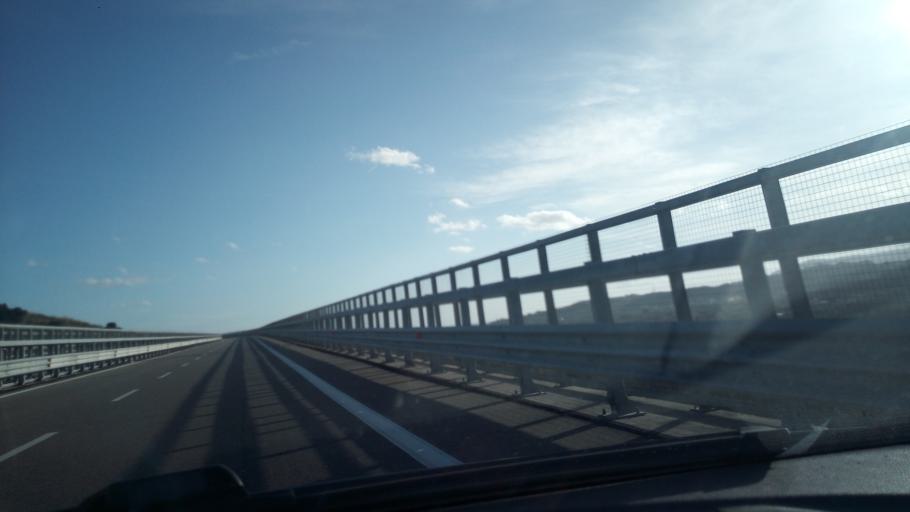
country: IT
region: Calabria
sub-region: Provincia di Catanzaro
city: Roccelletta
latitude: 38.8337
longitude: 16.5912
